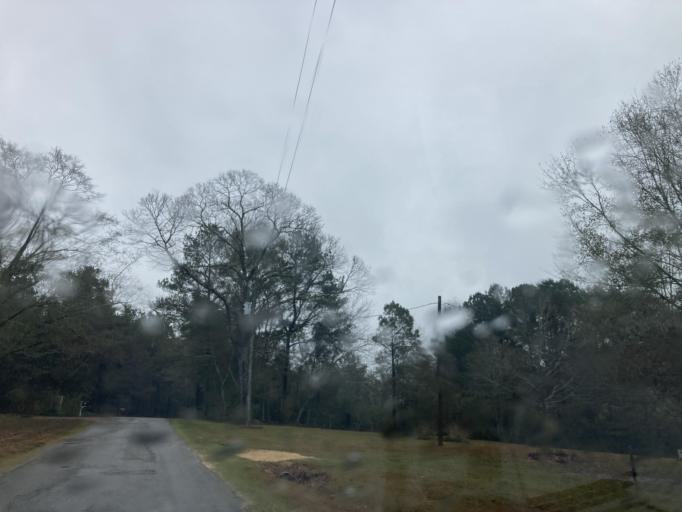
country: US
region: Mississippi
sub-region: Forrest County
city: Rawls Springs
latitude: 31.4828
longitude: -89.3847
